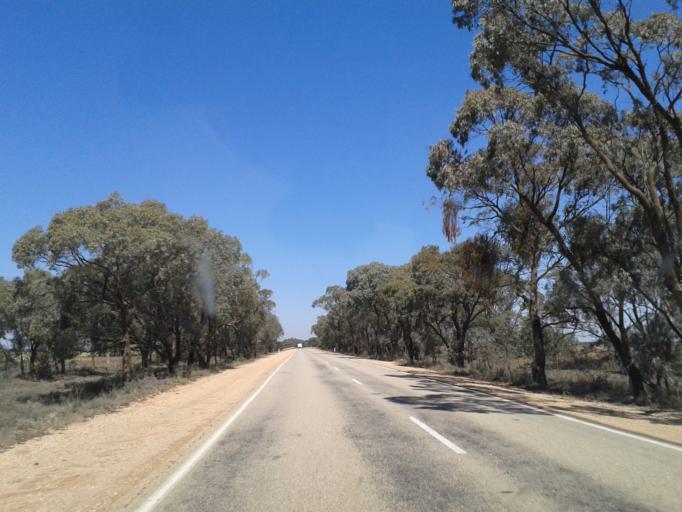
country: AU
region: Victoria
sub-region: Swan Hill
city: Swan Hill
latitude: -34.8995
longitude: 143.2980
